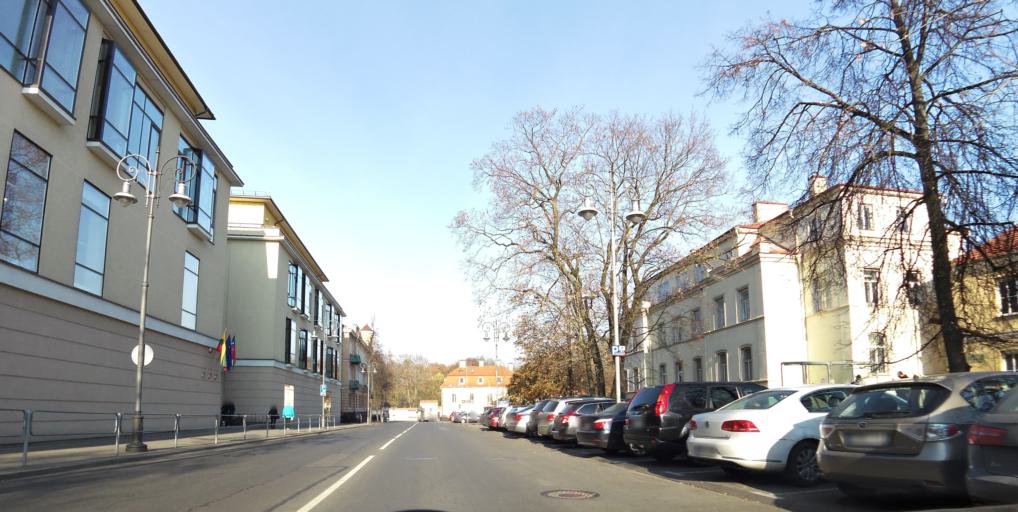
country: LT
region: Vilnius County
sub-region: Vilnius
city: Vilnius
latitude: 54.6838
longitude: 25.2929
